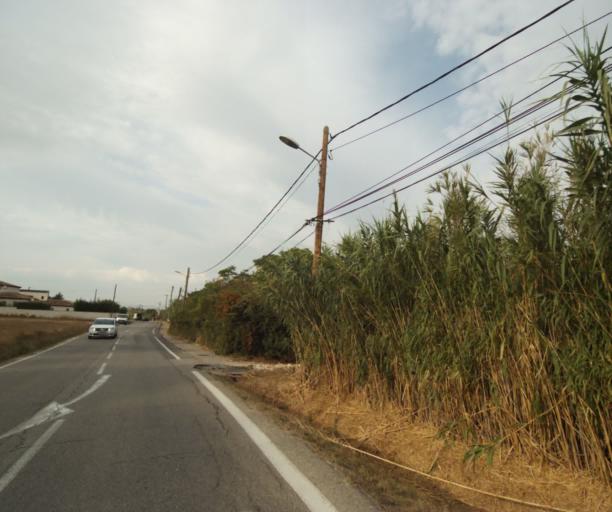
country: FR
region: Provence-Alpes-Cote d'Azur
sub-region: Departement des Bouches-du-Rhone
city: Gignac-la-Nerthe
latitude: 43.3964
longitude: 5.2196
